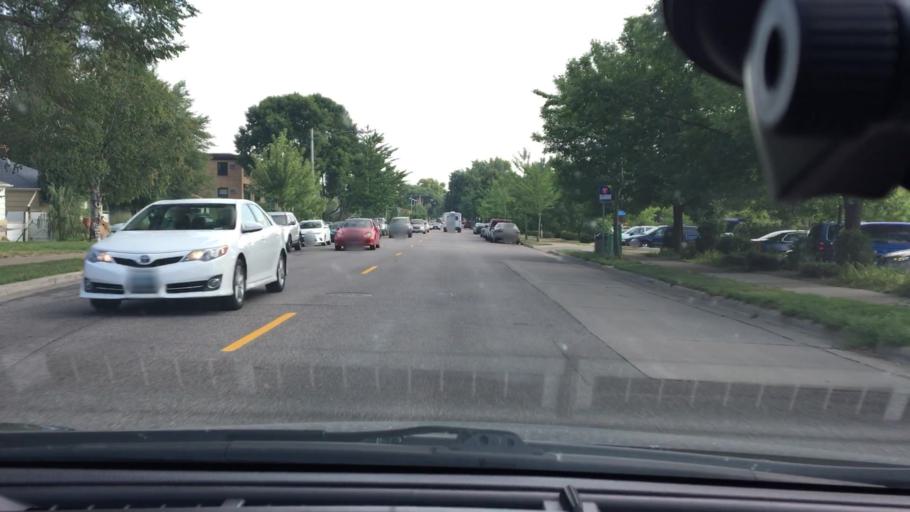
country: US
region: Minnesota
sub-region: Hennepin County
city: Minneapolis
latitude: 44.9304
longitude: -93.2524
